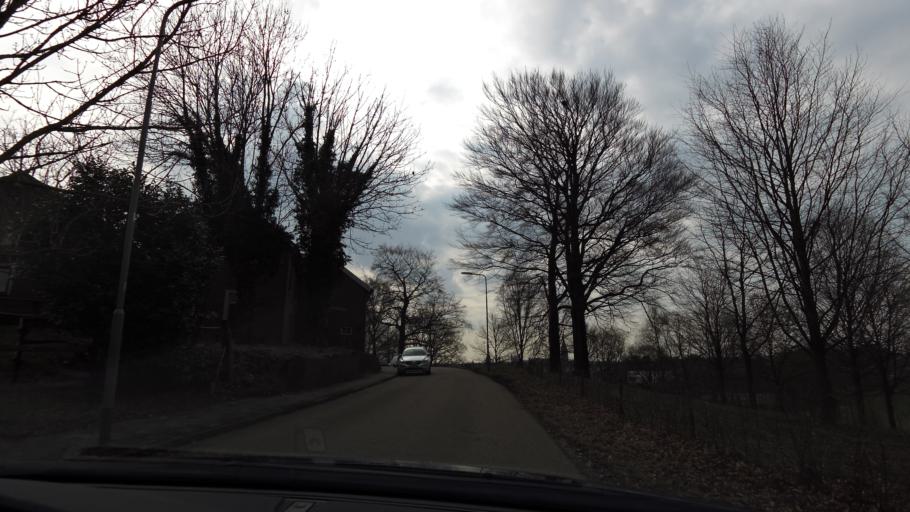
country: NL
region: Limburg
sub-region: Gemeente Simpelveld
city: Simpelveld
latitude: 50.8239
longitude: 6.0051
